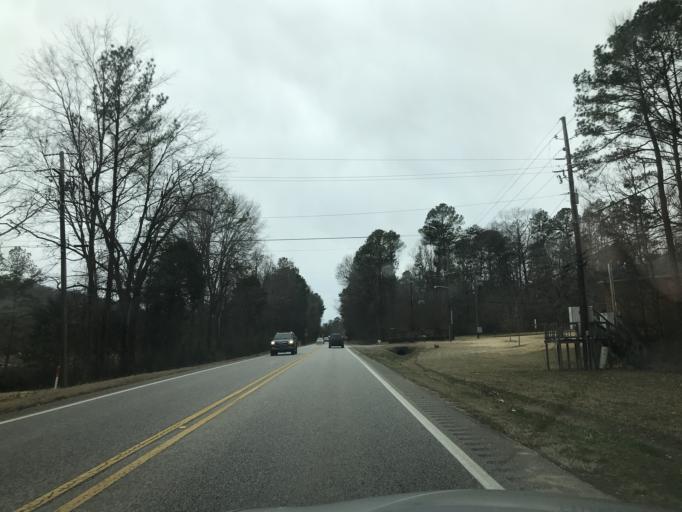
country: US
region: Alabama
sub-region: Shelby County
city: Meadowbrook
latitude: 33.3908
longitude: -86.6921
